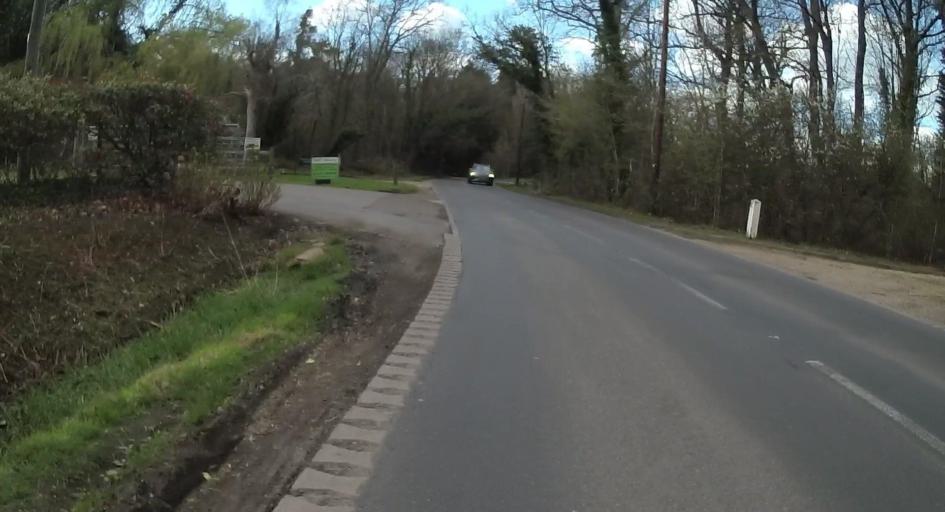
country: GB
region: England
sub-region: Surrey
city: Knaphill
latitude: 51.3354
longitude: -0.6264
